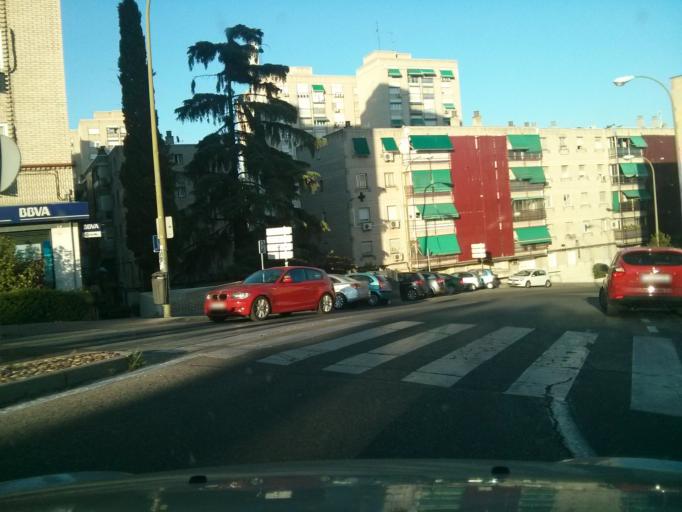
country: ES
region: Madrid
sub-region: Provincia de Madrid
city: Latina
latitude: 40.4044
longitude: -3.7515
